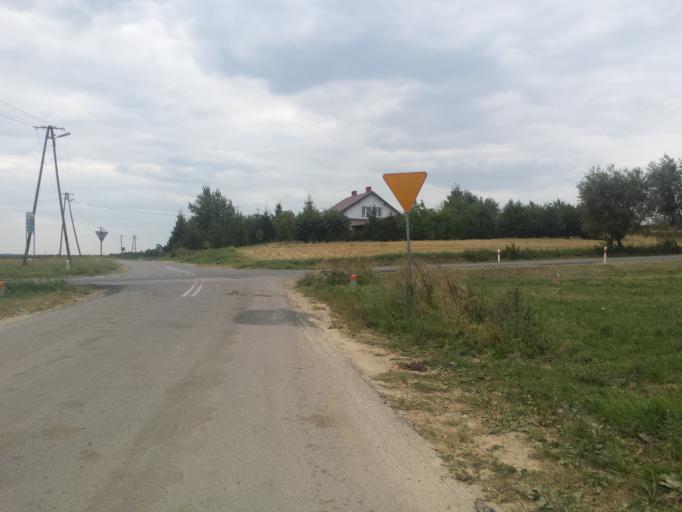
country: PL
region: Swietokrzyskie
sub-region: Powiat staszowski
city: Bogoria
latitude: 50.6868
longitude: 21.2401
